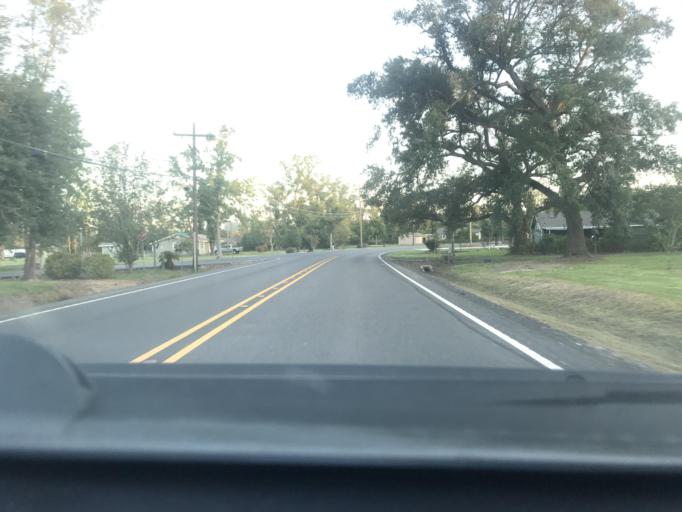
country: US
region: Louisiana
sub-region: Calcasieu Parish
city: Westlake
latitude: 30.2722
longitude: -93.2413
